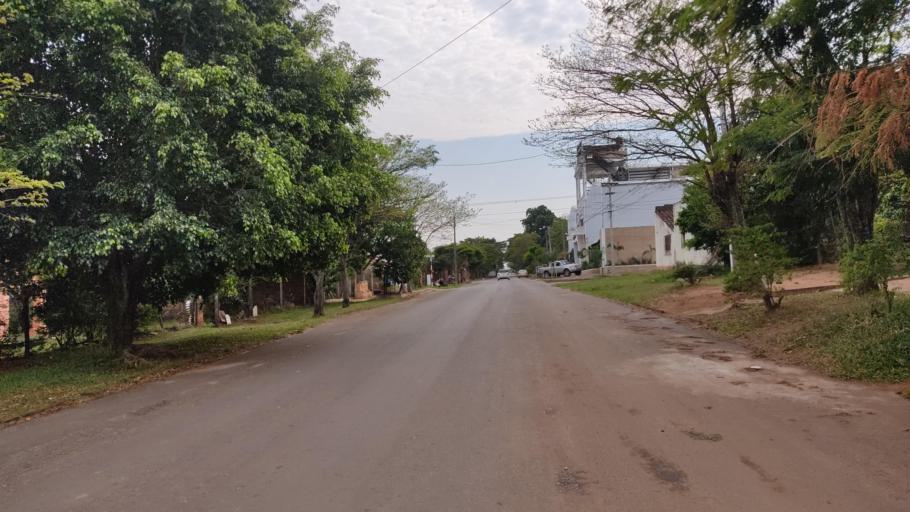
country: PY
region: Misiones
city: San Juan Bautista
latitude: -26.6711
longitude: -57.1518
